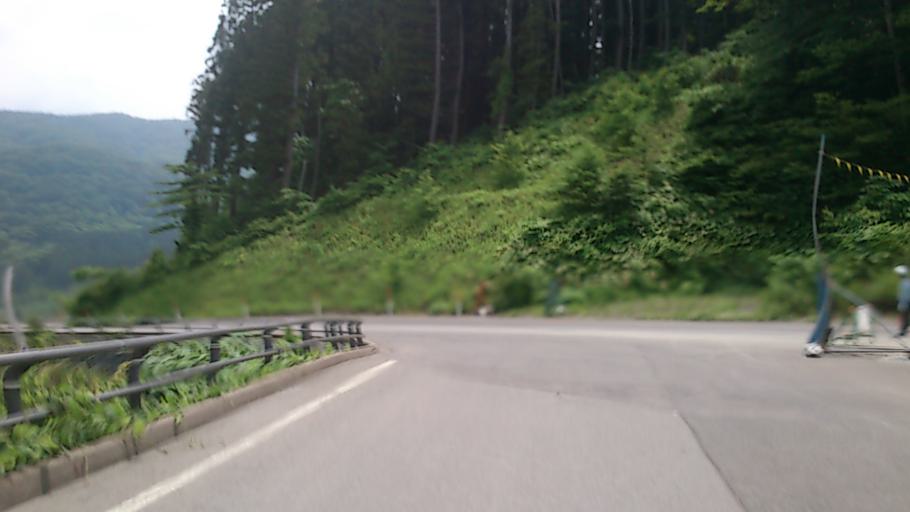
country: JP
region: Aomori
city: Hirosaki
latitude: 40.5361
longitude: 140.2621
